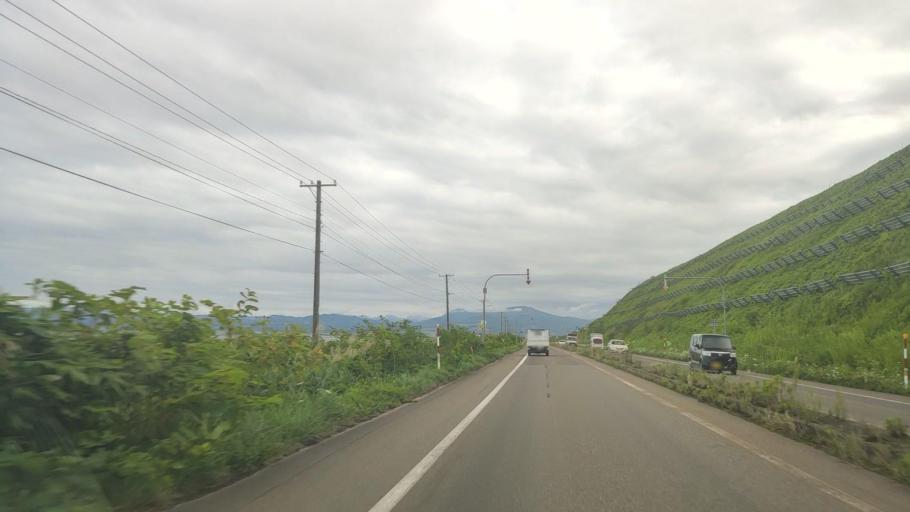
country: JP
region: Hokkaido
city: Niseko Town
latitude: 42.3287
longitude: 140.2773
